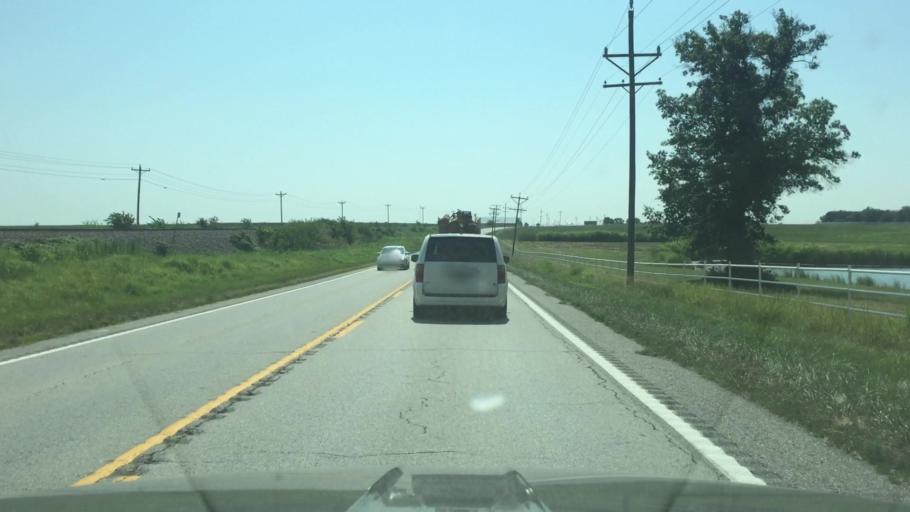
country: US
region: Missouri
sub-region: Moniteau County
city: Tipton
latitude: 38.6708
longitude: -92.8499
